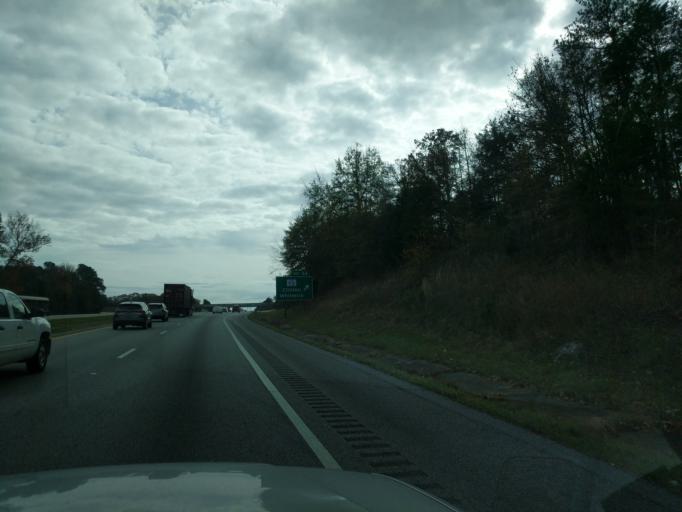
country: US
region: South Carolina
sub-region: Laurens County
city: Clinton
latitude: 34.5001
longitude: -81.8487
